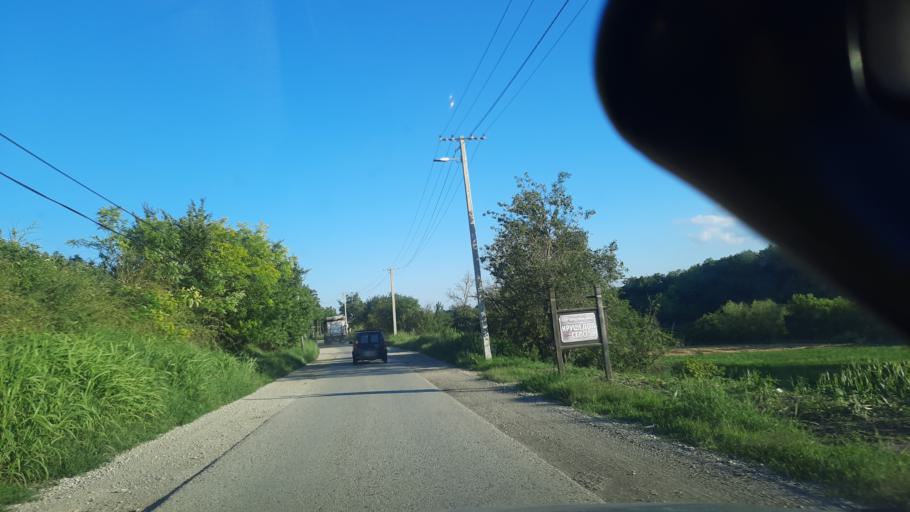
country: RS
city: Cortanovci
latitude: 45.1196
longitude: 19.9444
